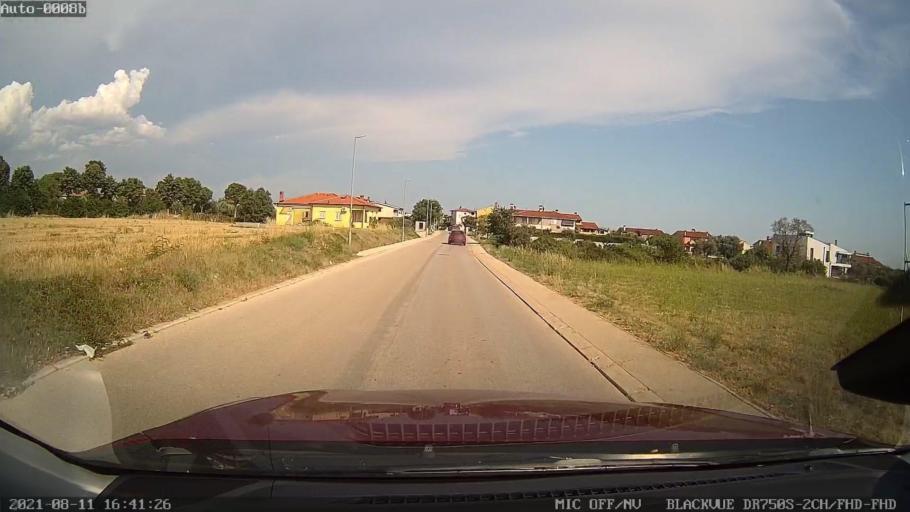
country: HR
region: Istarska
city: Vodnjan
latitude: 44.9557
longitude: 13.8456
